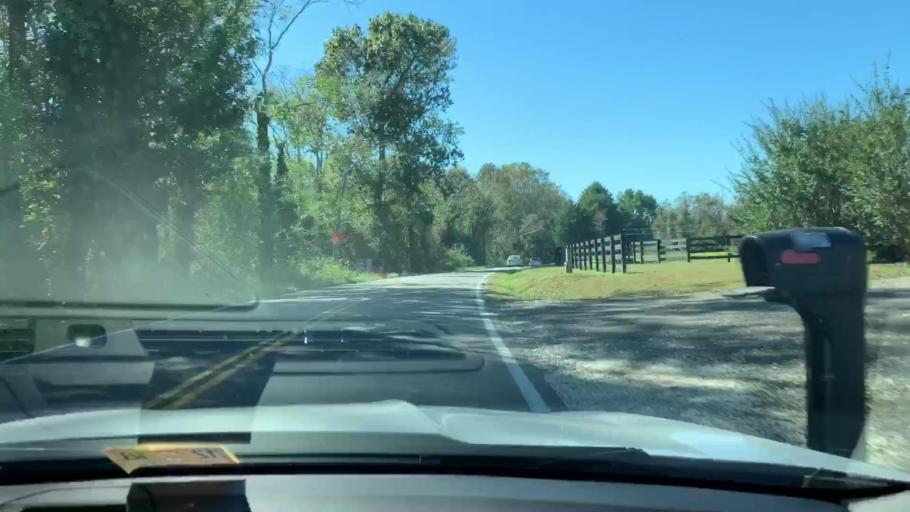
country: US
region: Virginia
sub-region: King William County
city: West Point
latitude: 37.4684
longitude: -76.8323
